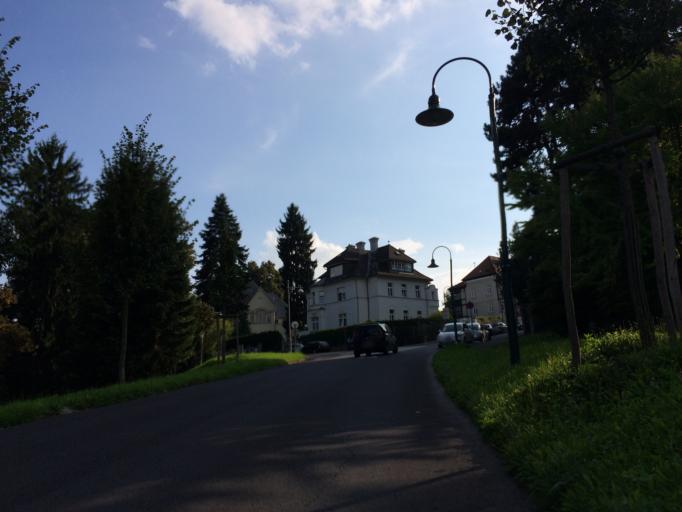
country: AT
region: Upper Austria
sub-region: Linz Stadt
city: Linz
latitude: 48.2975
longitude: 14.2818
